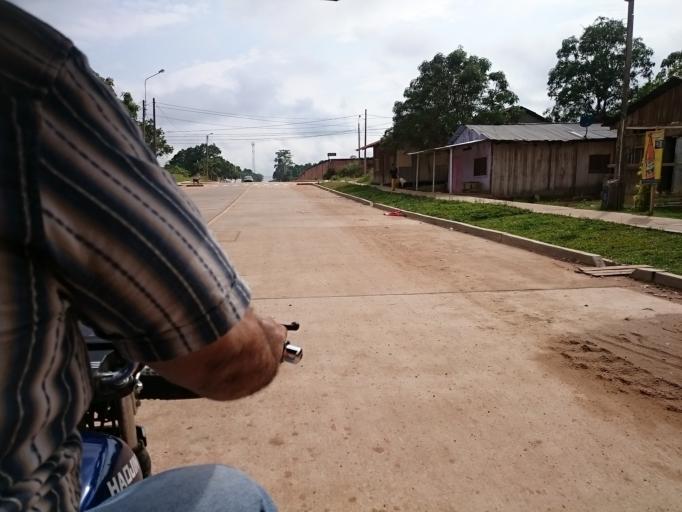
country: PE
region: Ucayali
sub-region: Provincia de Coronel Portillo
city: Puerto Callao
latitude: -8.3682
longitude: -74.5790
